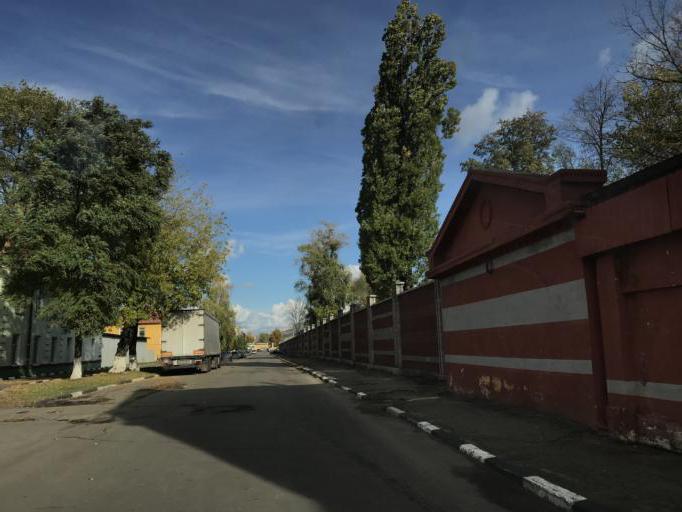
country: BY
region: Gomel
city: Gomel
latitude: 52.4491
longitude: 30.9735
